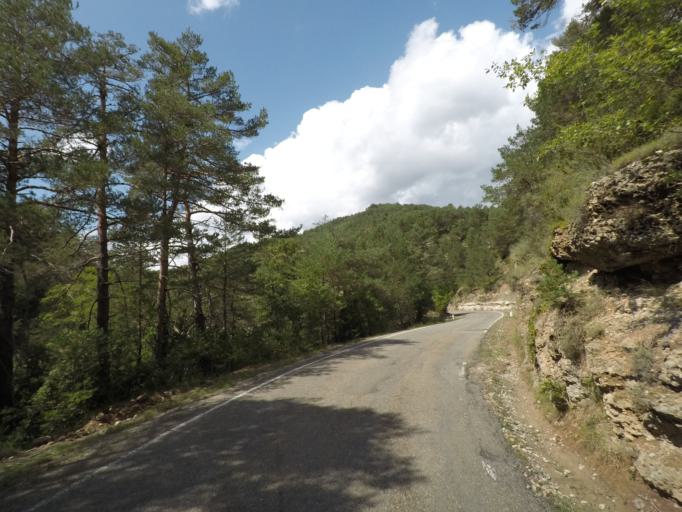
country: ES
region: Aragon
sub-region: Provincia de Huesca
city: Yebra de Basa
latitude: 42.4086
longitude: -0.2162
